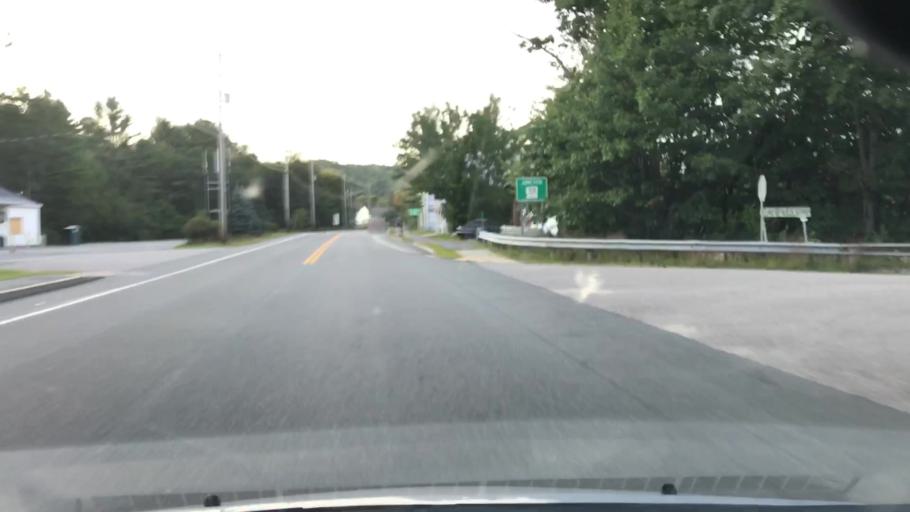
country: US
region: New Hampshire
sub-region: Grafton County
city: Rumney
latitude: 43.9199
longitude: -71.8891
